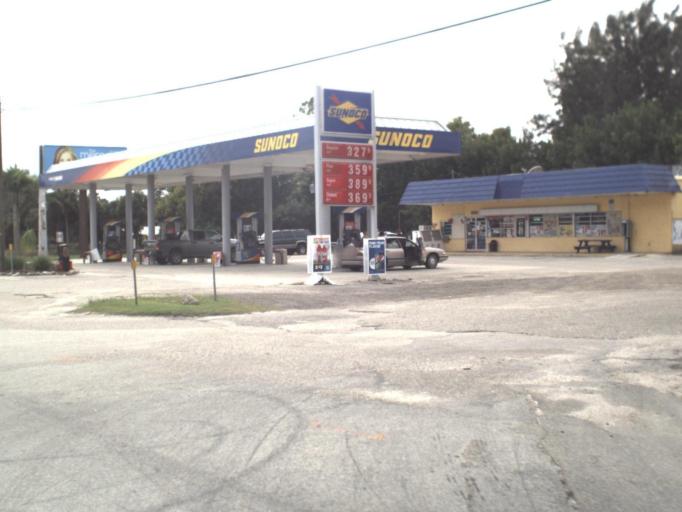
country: US
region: Florida
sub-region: Lee County
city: Fort Myers Shores
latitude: 26.7477
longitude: -81.7610
